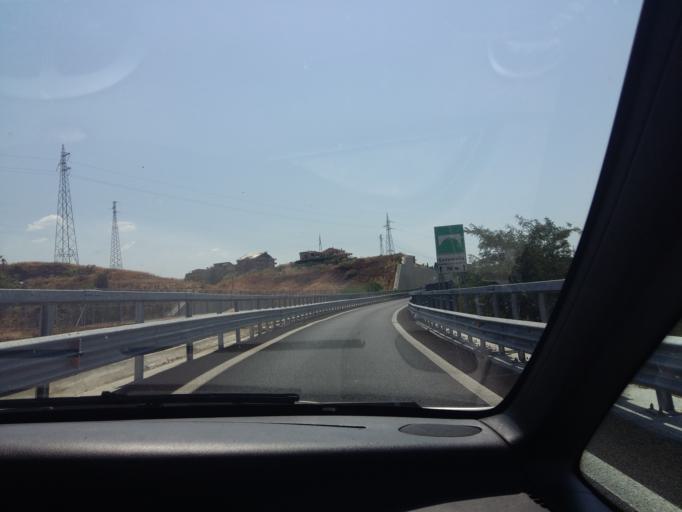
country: IT
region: Calabria
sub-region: Provincia di Reggio Calabria
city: Campo Calabro
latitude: 38.2220
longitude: 15.6474
